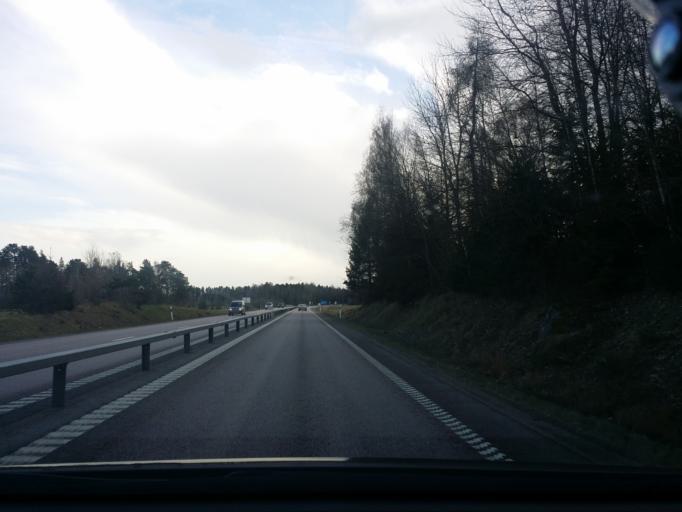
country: SE
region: Vaestmanland
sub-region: Vasteras
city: Hokasen
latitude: 59.6790
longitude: 16.5813
